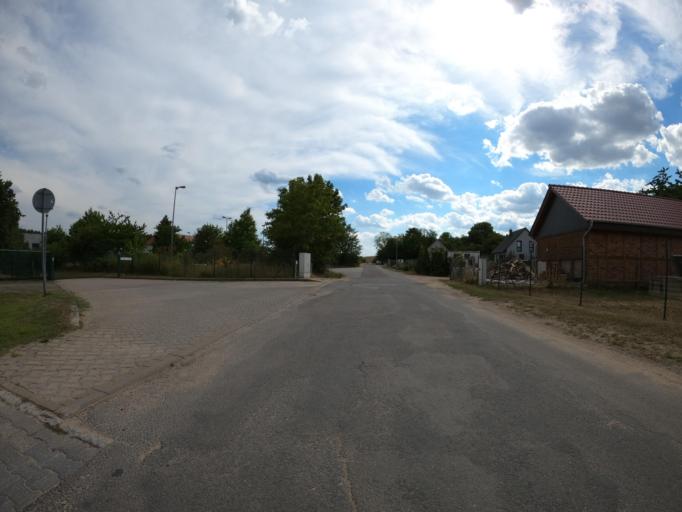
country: DE
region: Mecklenburg-Vorpommern
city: Loitz
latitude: 53.3276
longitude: 13.4305
